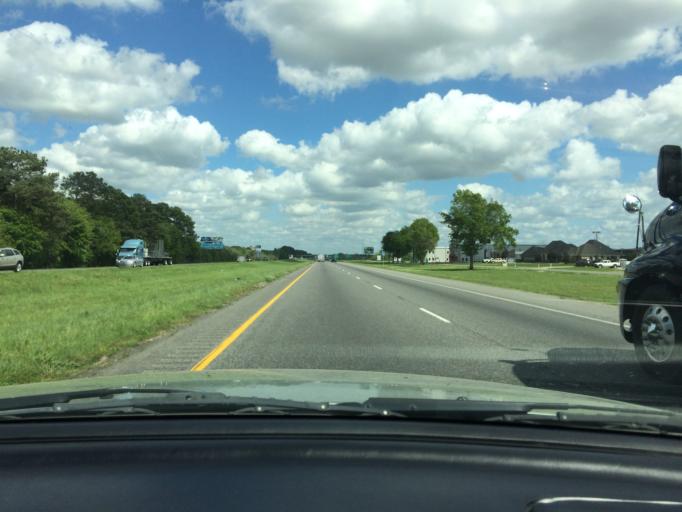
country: US
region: Louisiana
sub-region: Lafayette Parish
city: Scott
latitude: 30.2471
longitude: -92.1014
